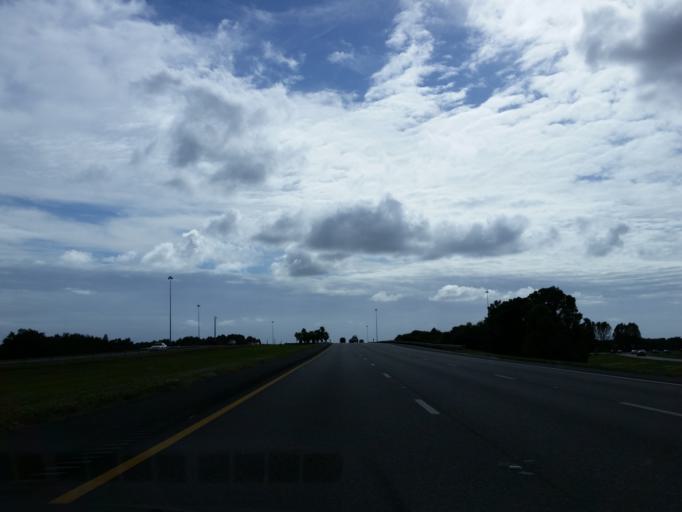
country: US
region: Florida
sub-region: Sarasota County
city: Lake Sarasota
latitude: 27.2726
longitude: -82.4491
